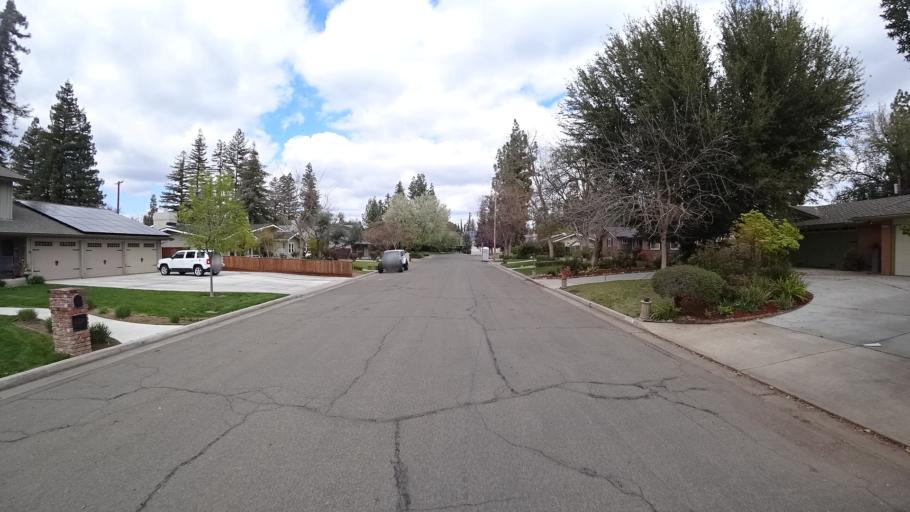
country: US
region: California
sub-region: Fresno County
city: Fresno
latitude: 36.8268
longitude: -119.8394
